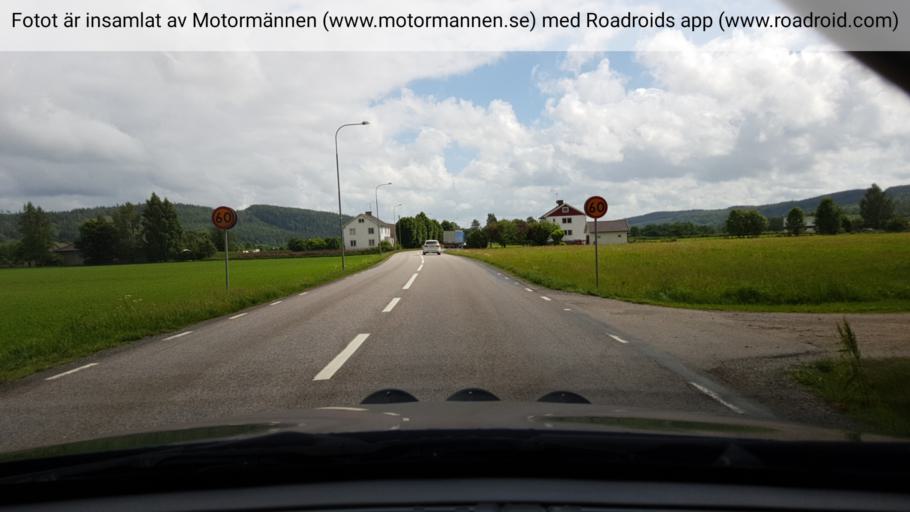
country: SE
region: Vaestra Goetaland
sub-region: Marks Kommun
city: Horred
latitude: 57.4236
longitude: 12.5215
